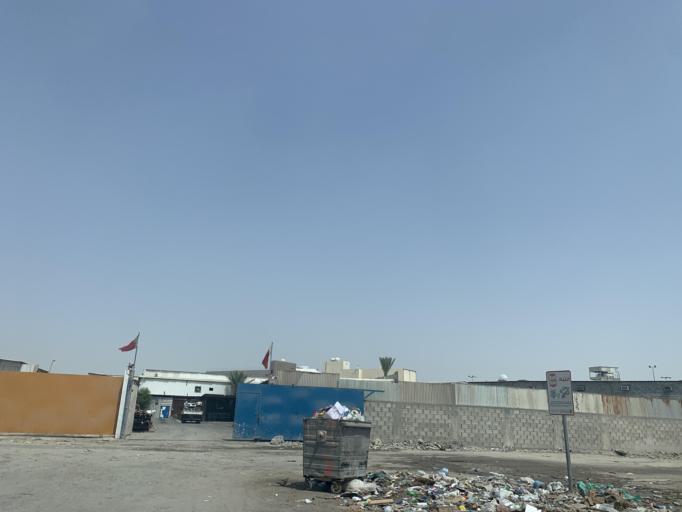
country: BH
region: Central Governorate
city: Madinat Hamad
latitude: 26.1404
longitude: 50.4874
